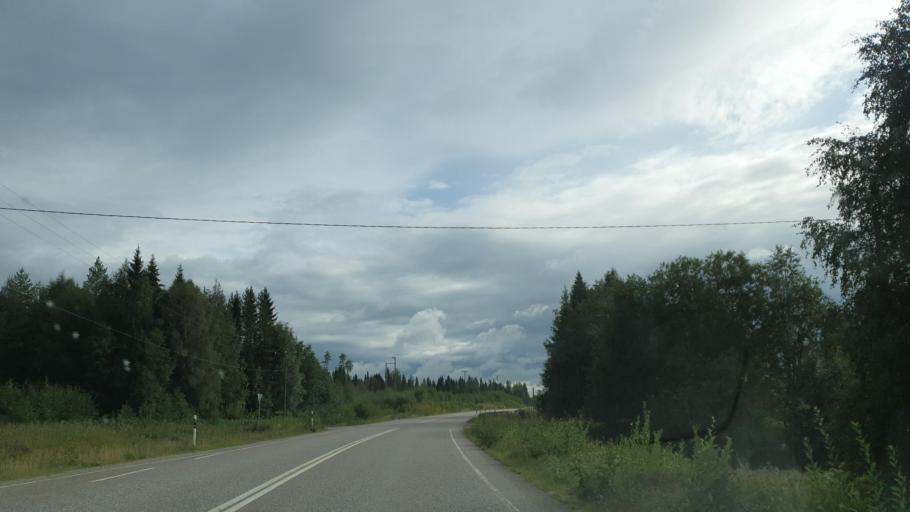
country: FI
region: Kainuu
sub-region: Kehys-Kainuu
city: Puolanka
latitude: 64.7635
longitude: 27.7848
